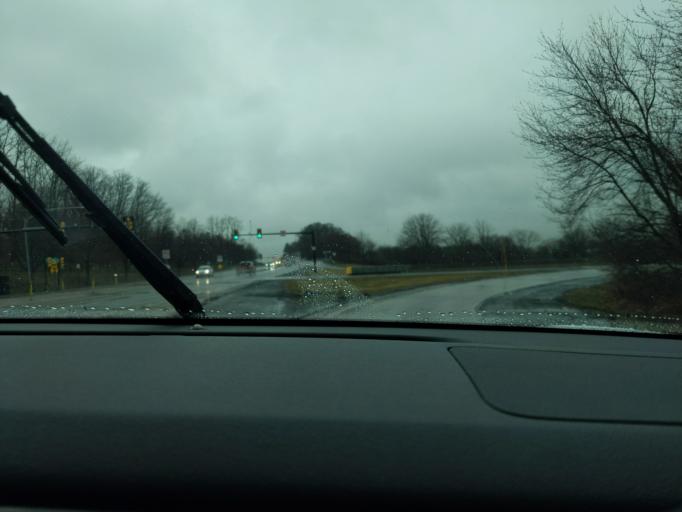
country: US
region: Pennsylvania
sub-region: Bucks County
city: Doylestown
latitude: 40.3041
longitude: -75.1464
